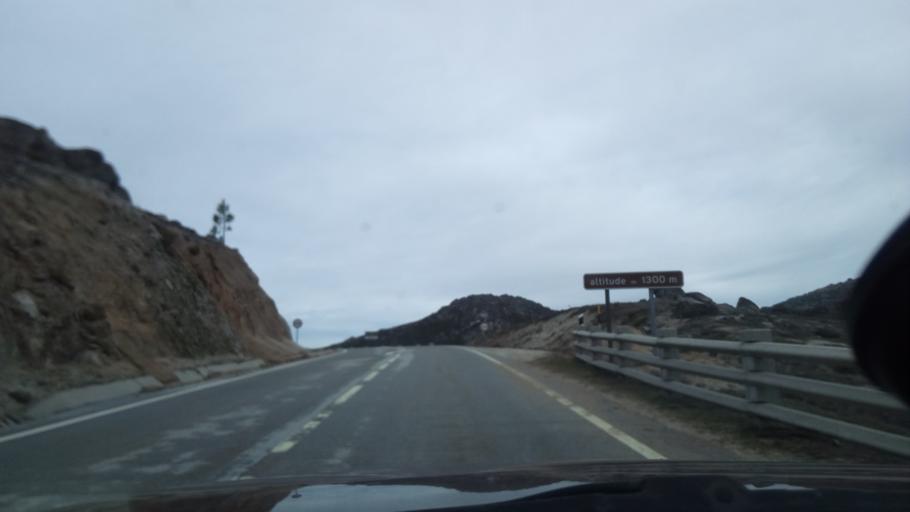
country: PT
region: Guarda
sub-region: Seia
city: Seia
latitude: 40.3453
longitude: -7.6935
